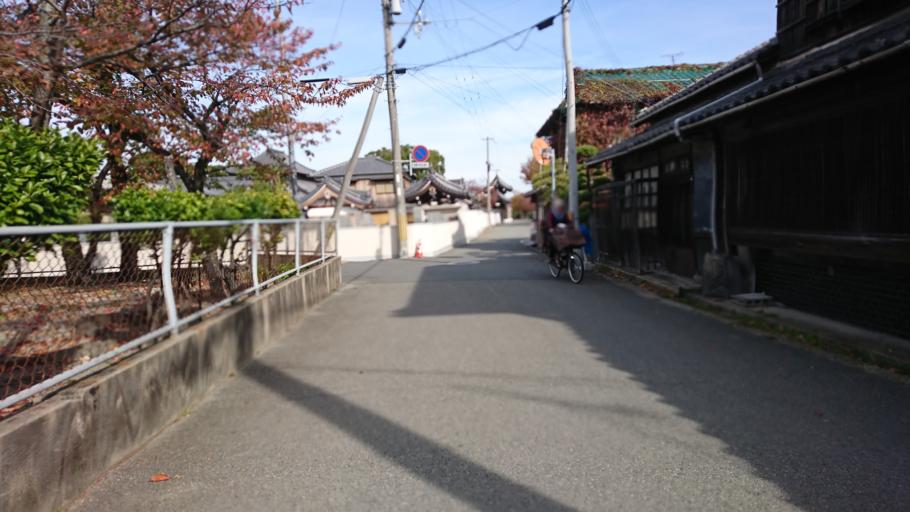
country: JP
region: Hyogo
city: Kakogawacho-honmachi
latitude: 34.7462
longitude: 134.7997
